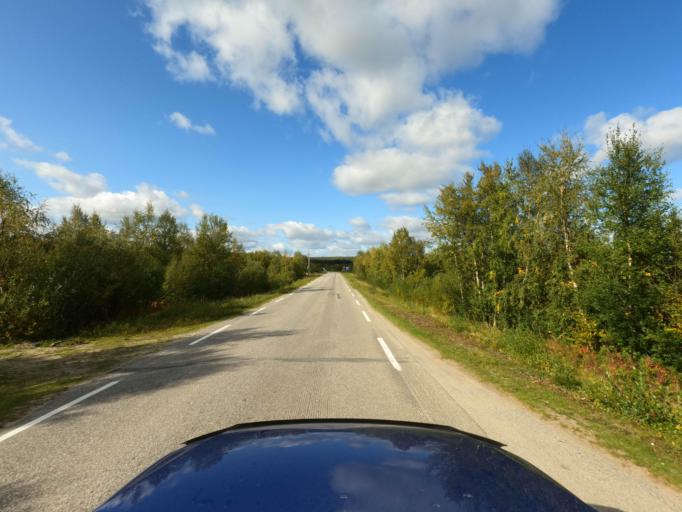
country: NO
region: Finnmark Fylke
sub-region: Karasjok
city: Karasjohka
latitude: 69.3999
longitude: 25.8309
